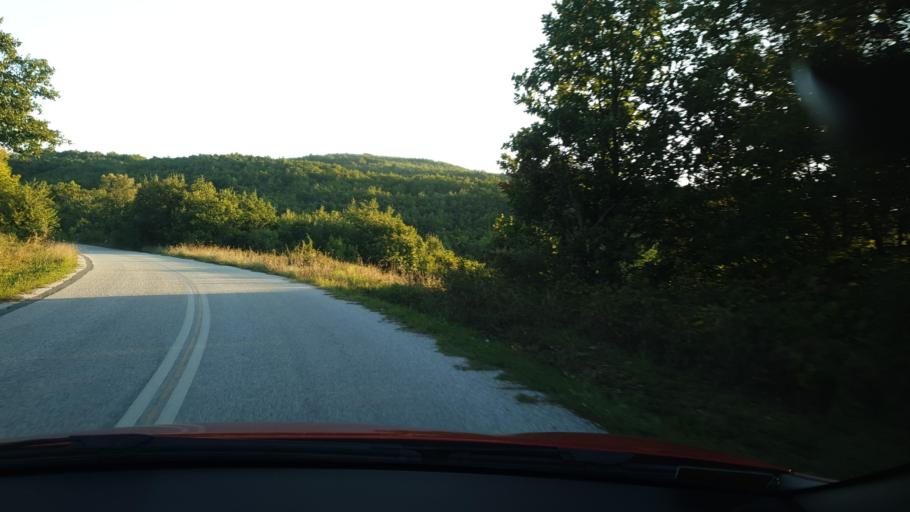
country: GR
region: Central Macedonia
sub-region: Nomos Chalkidikis
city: Galatista
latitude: 40.5188
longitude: 23.2715
